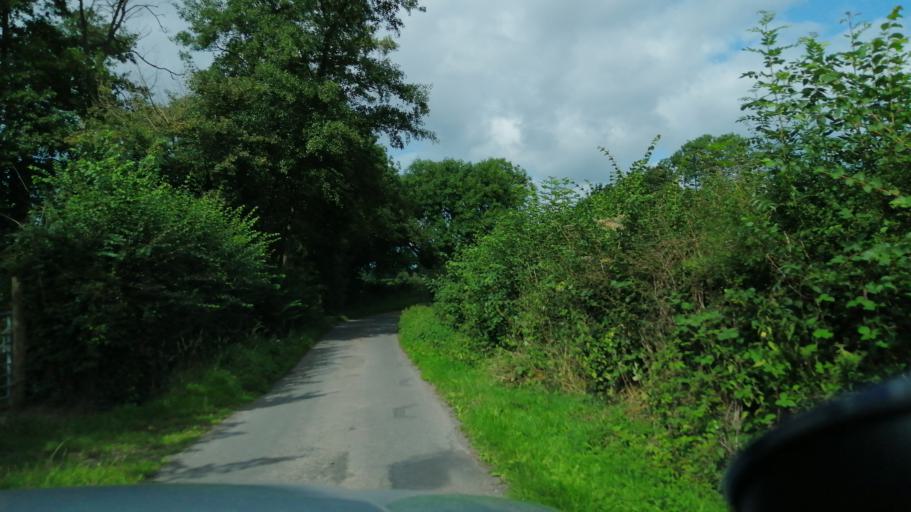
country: GB
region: England
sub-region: Herefordshire
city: Kinnersley
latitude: 52.1324
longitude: -2.9389
